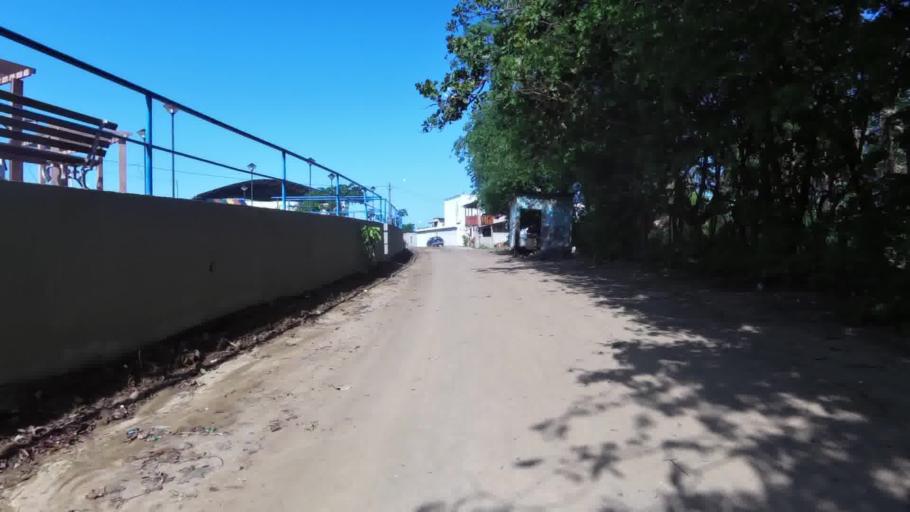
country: BR
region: Espirito Santo
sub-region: Piuma
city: Piuma
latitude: -20.8243
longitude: -40.6249
